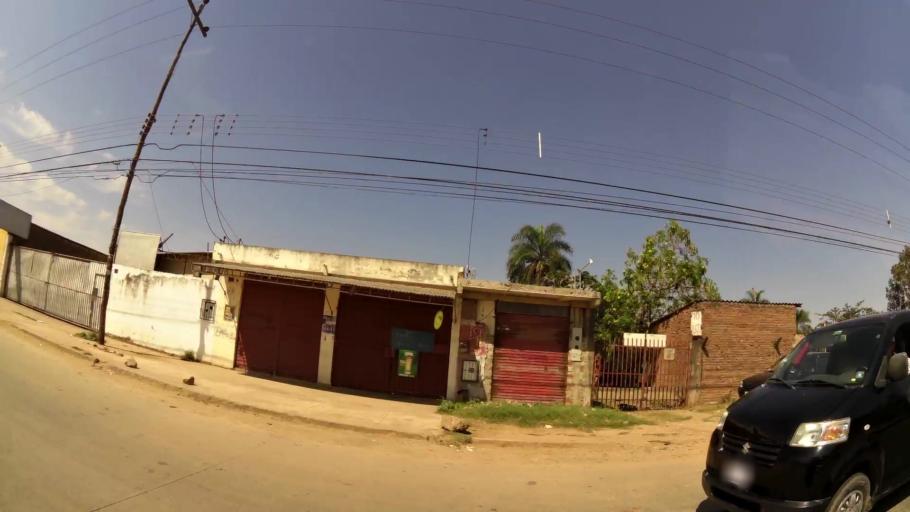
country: BO
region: Santa Cruz
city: Santa Cruz de la Sierra
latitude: -17.7330
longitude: -63.1513
